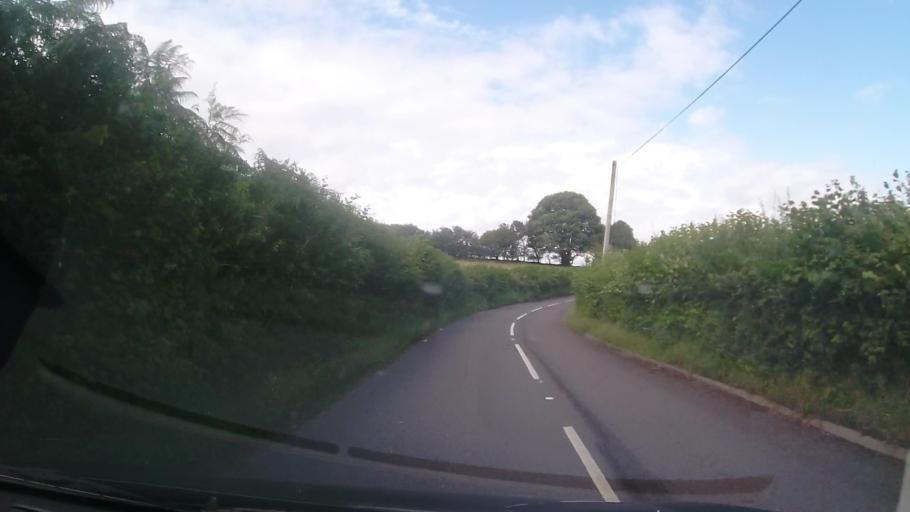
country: GB
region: England
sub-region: Shropshire
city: Acton
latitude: 52.4143
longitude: -3.0398
